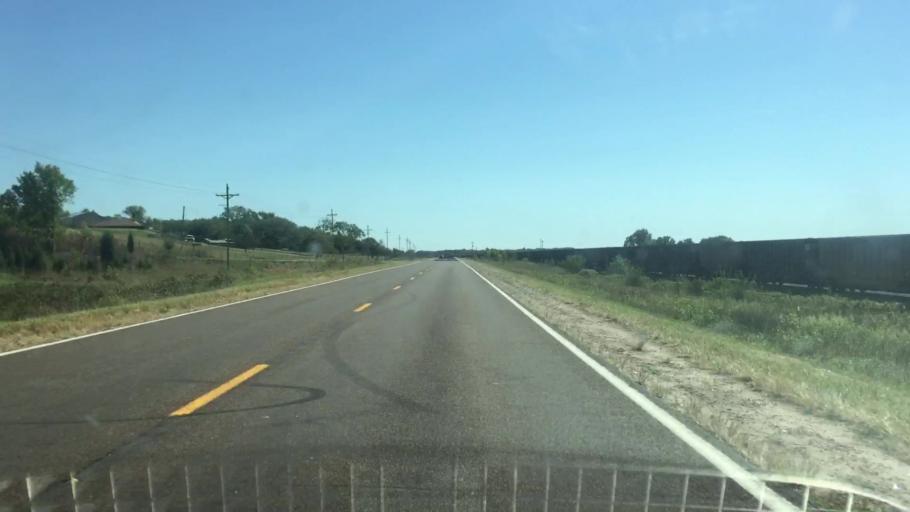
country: US
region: Nebraska
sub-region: Jefferson County
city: Fairbury
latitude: 40.0918
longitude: -97.1252
